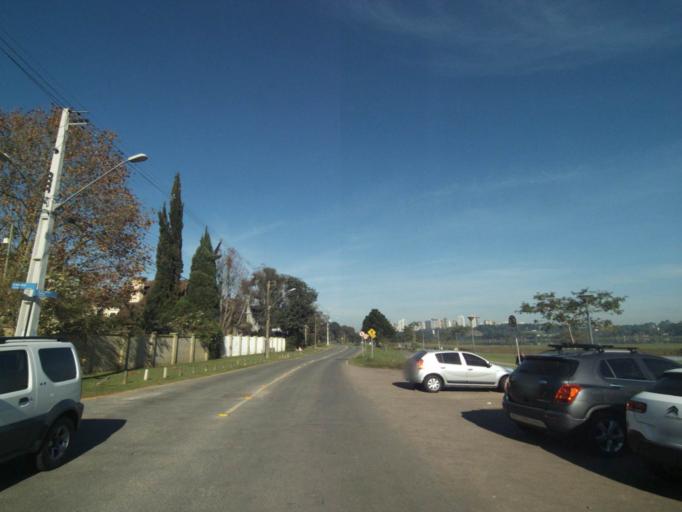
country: BR
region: Parana
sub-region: Curitiba
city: Curitiba
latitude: -25.4289
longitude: -49.3059
